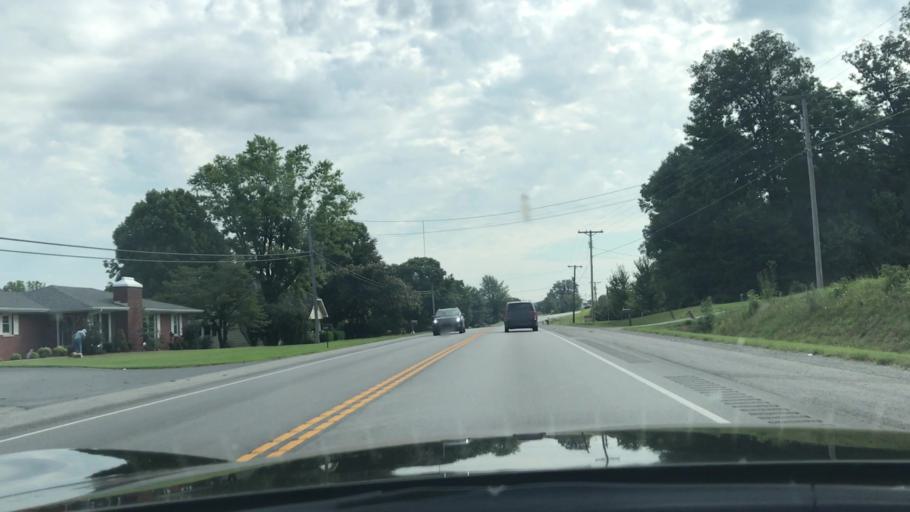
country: US
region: Kentucky
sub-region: Taylor County
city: Campbellsville
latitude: 37.3302
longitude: -85.3843
